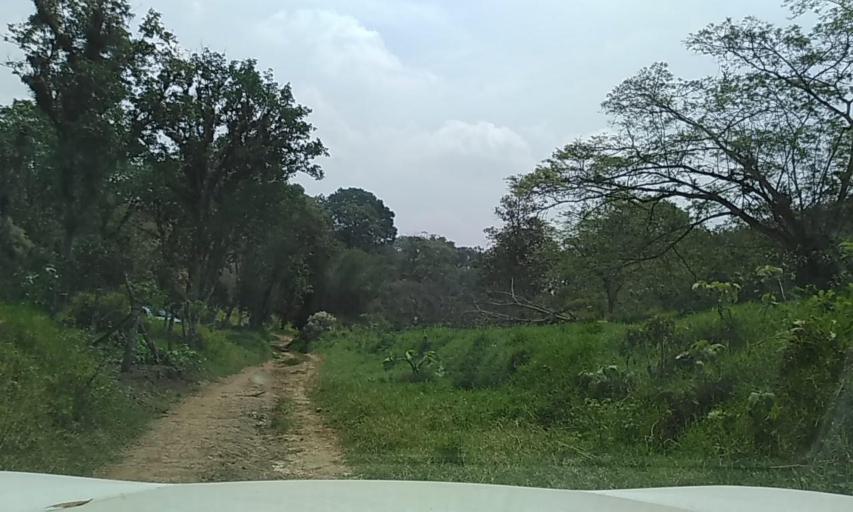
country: MX
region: Veracruz
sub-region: Xalapa
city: Fraccionamiento las Fuentes
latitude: 19.4915
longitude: -96.8952
